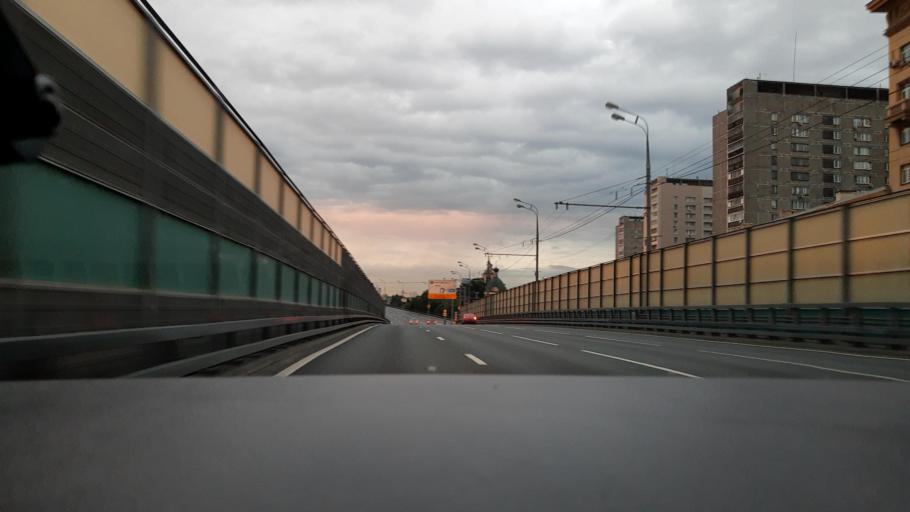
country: RU
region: Moscow
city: Ostankinskiy
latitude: 55.8260
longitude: 37.6074
